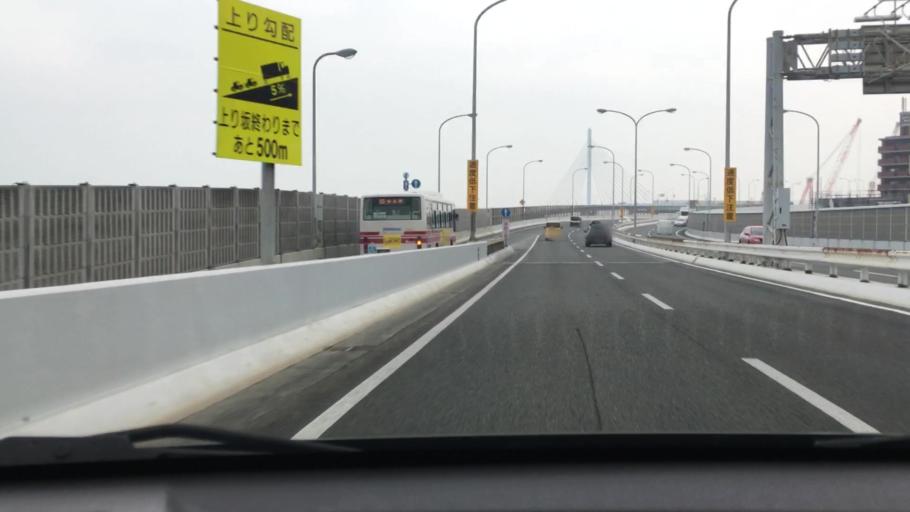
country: JP
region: Fukuoka
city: Fukuoka-shi
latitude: 33.6002
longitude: 130.3754
